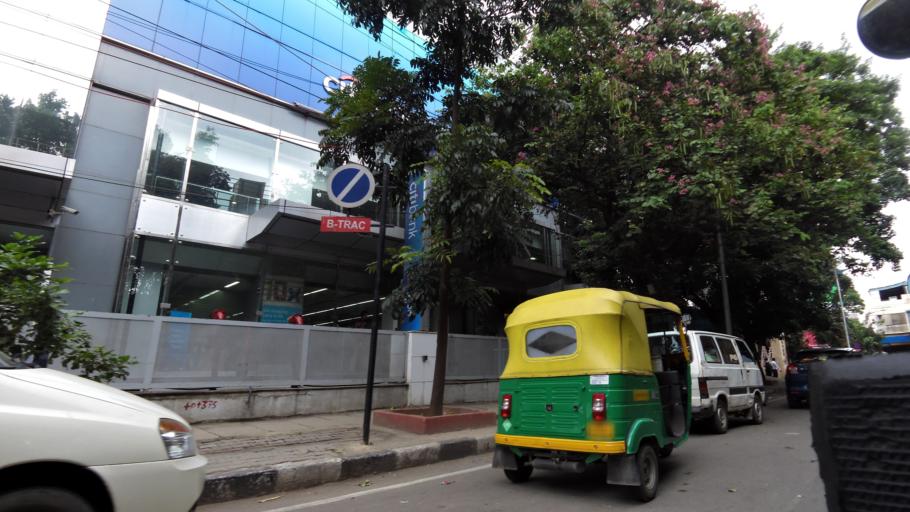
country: IN
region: Karnataka
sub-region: Bangalore Urban
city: Bangalore
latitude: 12.9735
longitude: 77.6154
